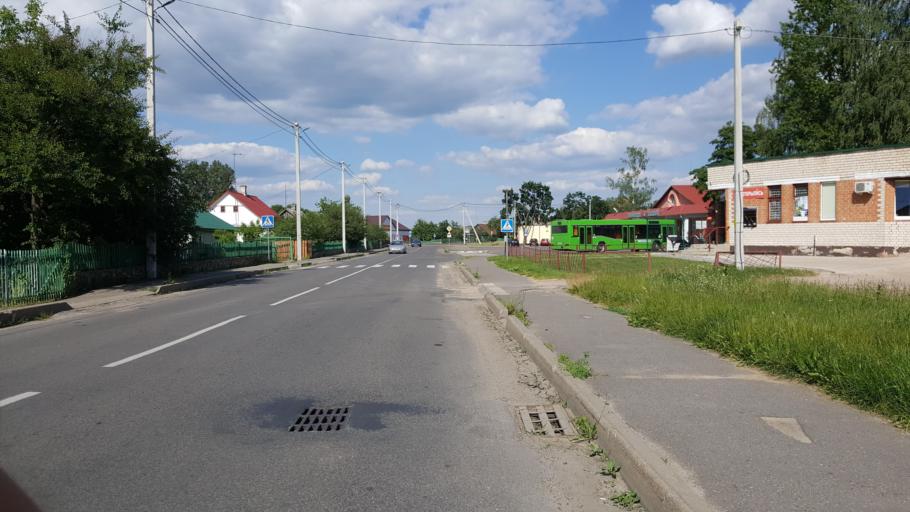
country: BY
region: Brest
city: Kamyanyets
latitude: 52.4032
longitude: 23.8111
